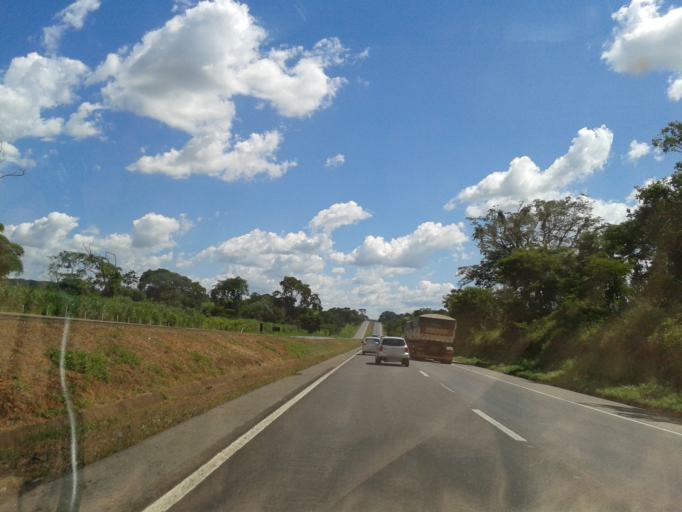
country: BR
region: Goias
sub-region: Piracanjuba
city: Piracanjuba
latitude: -17.4128
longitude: -49.2257
